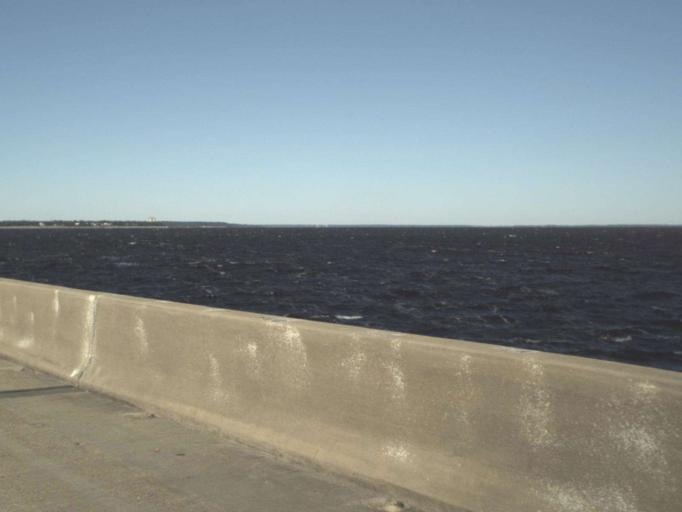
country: US
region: Florida
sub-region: Santa Rosa County
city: Gulf Breeze
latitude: 30.3854
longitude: -87.1816
